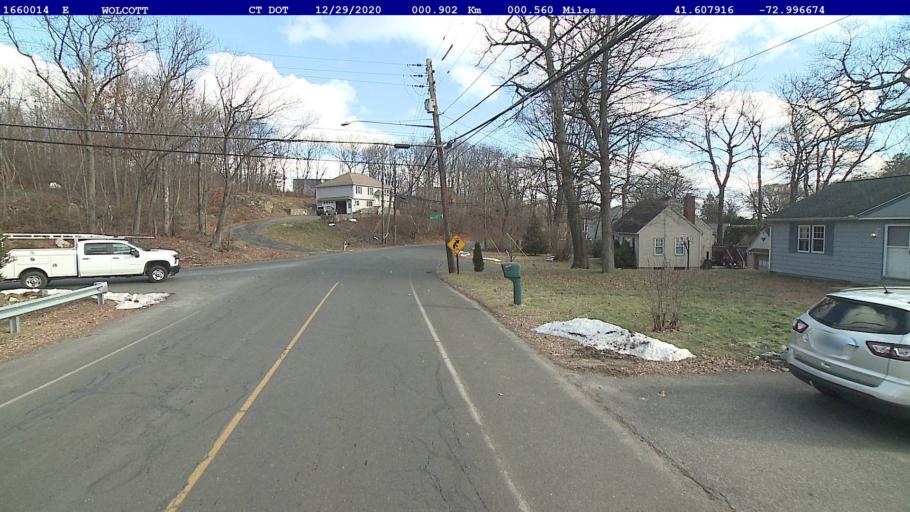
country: US
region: Connecticut
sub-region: New Haven County
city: Wolcott
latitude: 41.6079
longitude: -72.9967
